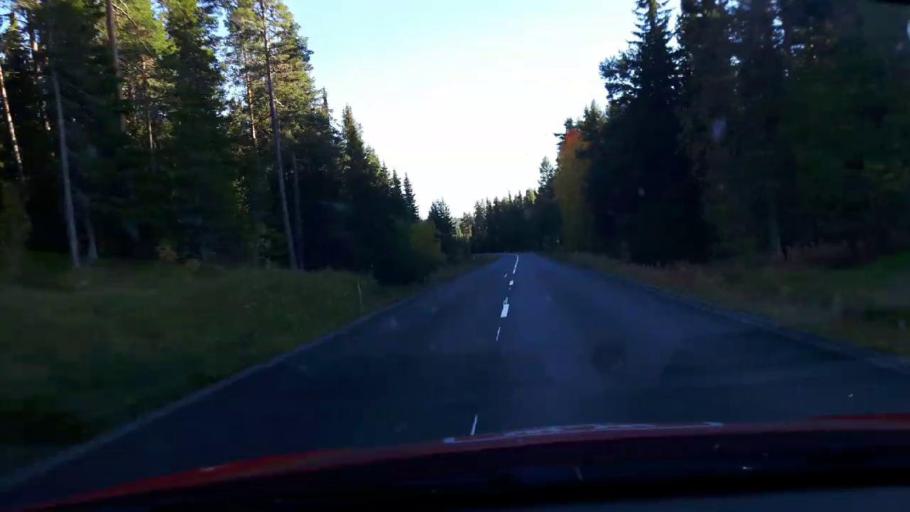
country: SE
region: Jaemtland
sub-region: OEstersunds Kommun
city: Lit
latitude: 63.5277
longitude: 14.8448
